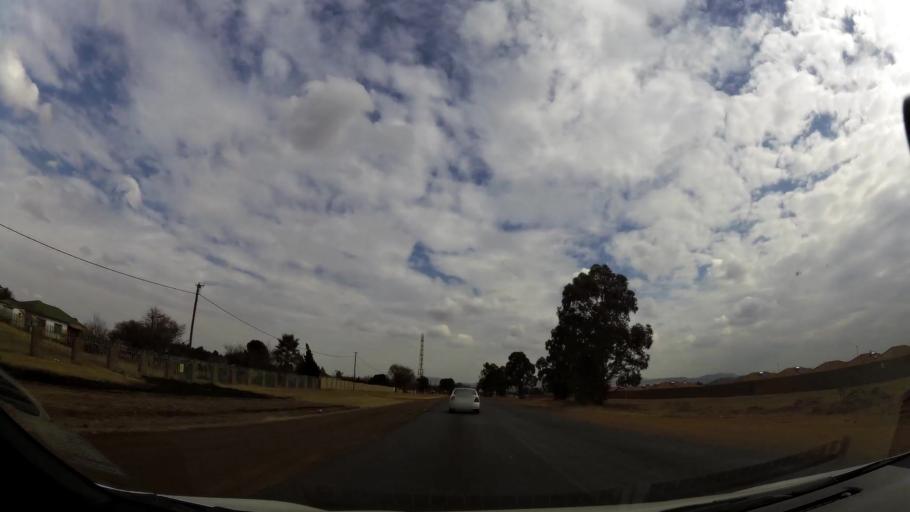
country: ZA
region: Gauteng
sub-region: Sedibeng District Municipality
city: Meyerton
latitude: -26.4195
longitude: 28.1117
